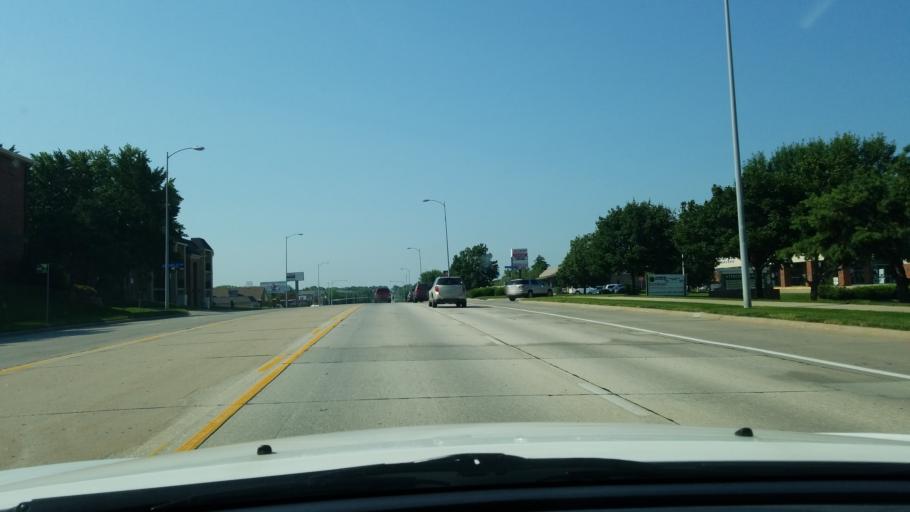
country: US
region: Nebraska
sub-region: Lancaster County
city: Lincoln
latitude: 40.7867
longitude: -96.6252
